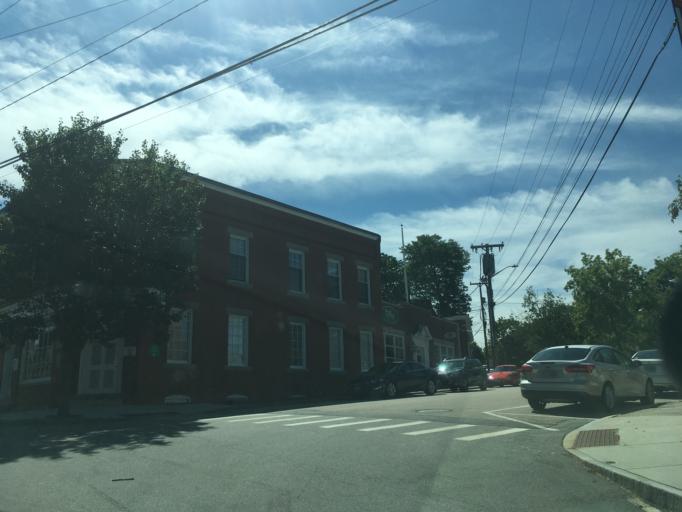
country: US
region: New Hampshire
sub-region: Rockingham County
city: Exeter
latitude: 42.9818
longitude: -70.9484
